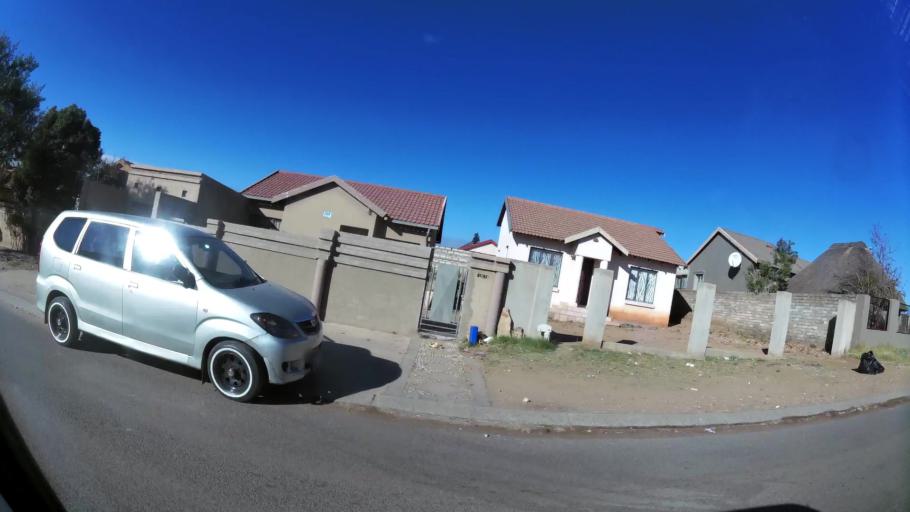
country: ZA
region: Gauteng
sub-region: City of Johannesburg Metropolitan Municipality
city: Diepsloot
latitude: -25.9067
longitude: 28.0960
